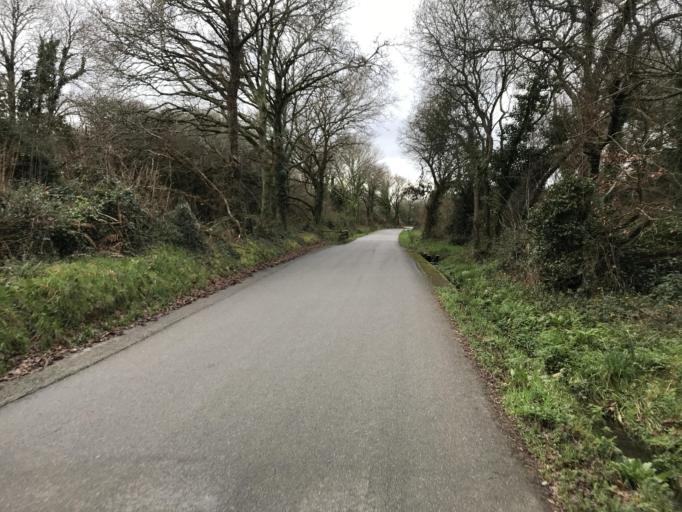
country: FR
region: Brittany
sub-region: Departement du Finistere
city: Plougastel-Daoulas
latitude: 48.3737
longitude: -4.3542
